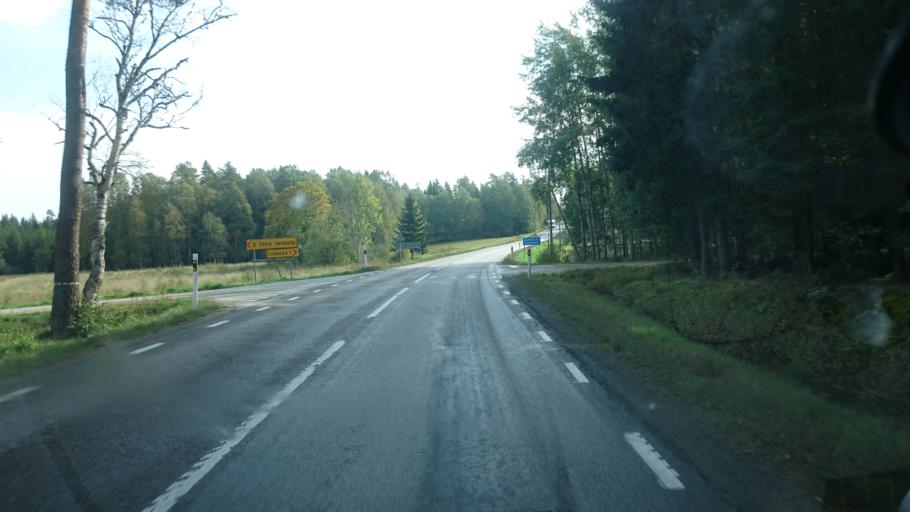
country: SE
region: Vaestra Goetaland
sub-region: Alingsas Kommun
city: Sollebrunn
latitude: 58.1334
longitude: 12.4823
